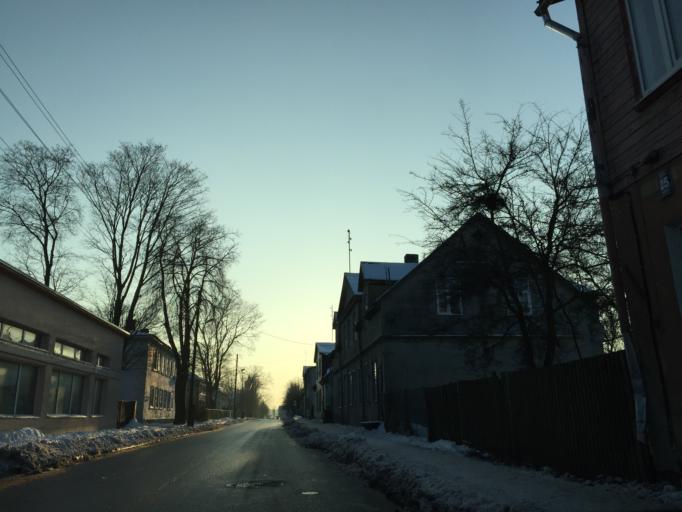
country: LV
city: Tireli
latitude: 56.9451
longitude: 23.6163
